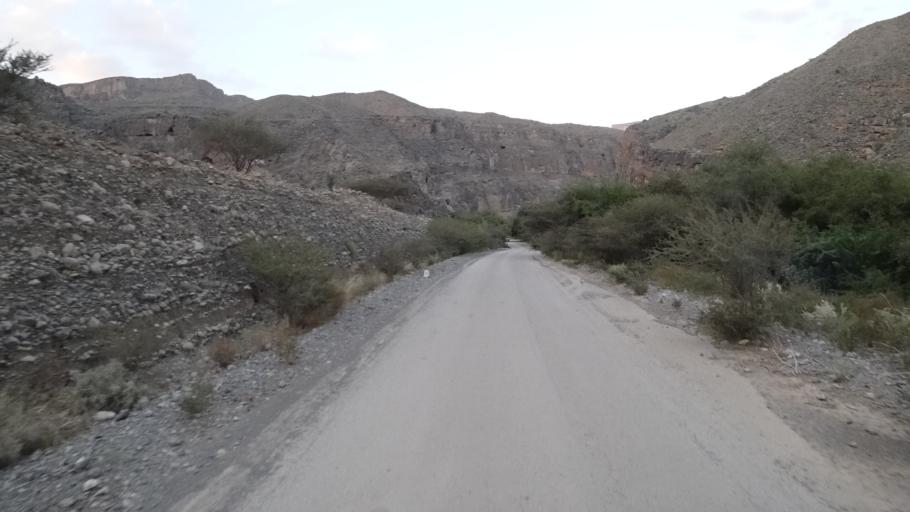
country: OM
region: Muhafazat ad Dakhiliyah
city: Nizwa
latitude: 23.0638
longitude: 57.4688
